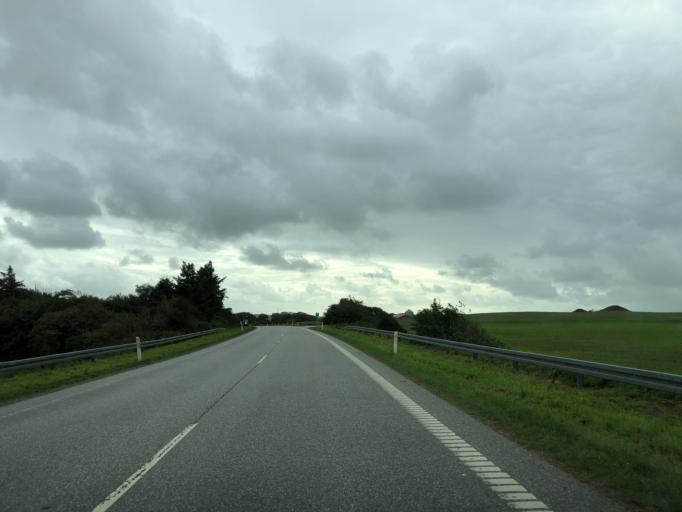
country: DK
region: North Denmark
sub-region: Thisted Kommune
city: Hurup
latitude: 56.8016
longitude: 8.4741
